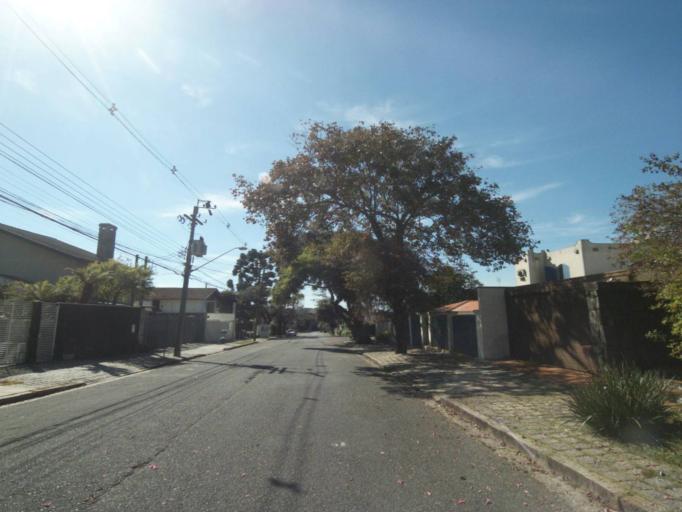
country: BR
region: Parana
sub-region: Curitiba
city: Curitiba
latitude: -25.4184
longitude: -49.2352
